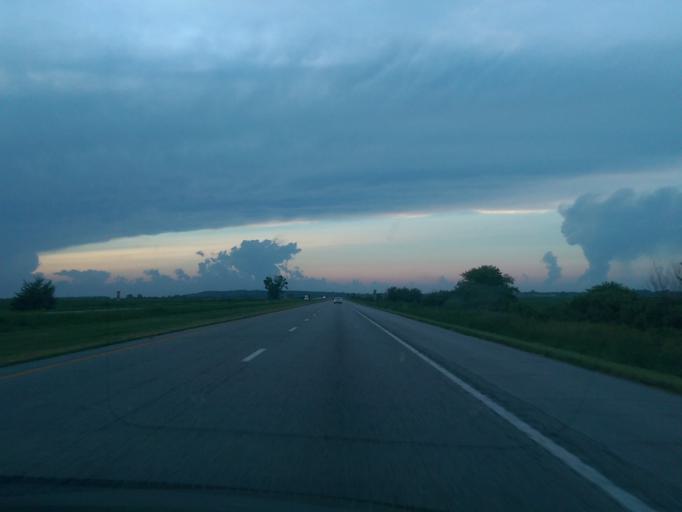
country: US
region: Iowa
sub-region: Fremont County
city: Hamburg
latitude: 40.5019
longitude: -95.5995
